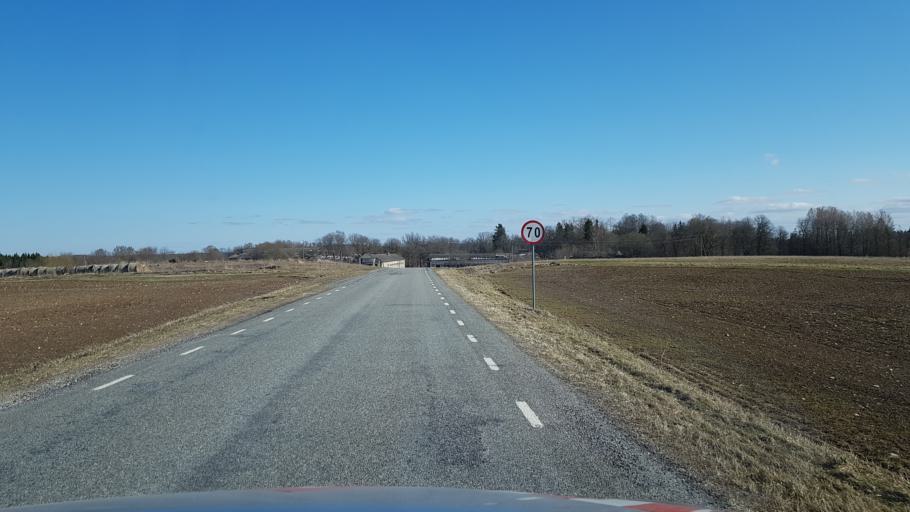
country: EE
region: Laeaene-Virumaa
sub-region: Kadrina vald
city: Kadrina
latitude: 59.3779
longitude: 26.0352
